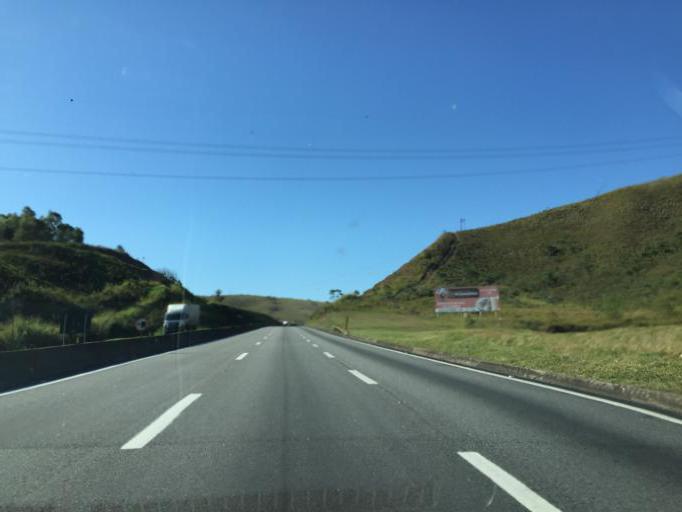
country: BR
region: Sao Paulo
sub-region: Cruzeiro
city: Cruzeiro
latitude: -22.6437
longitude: -44.9488
